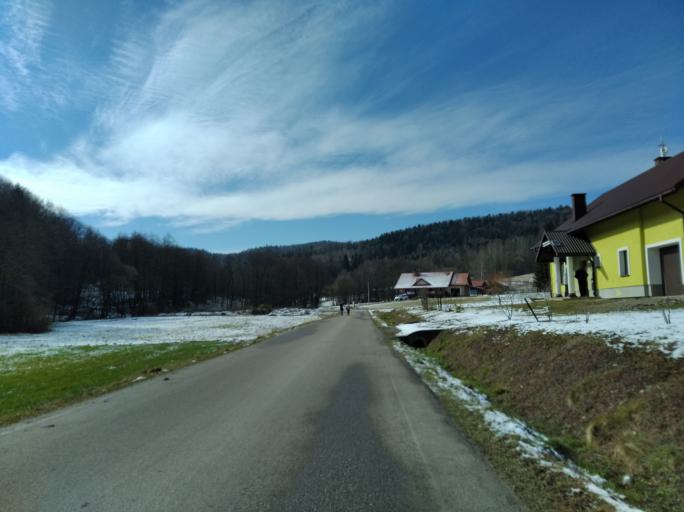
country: PL
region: Subcarpathian Voivodeship
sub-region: Powiat brzozowski
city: Jablonica Polska
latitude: 49.7521
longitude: 21.8837
